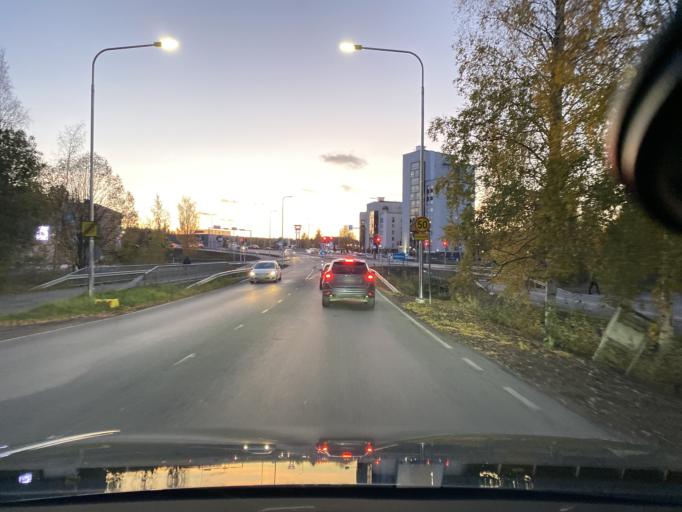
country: FI
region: Pirkanmaa
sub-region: Tampere
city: Tampere
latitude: 61.4707
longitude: 23.7241
